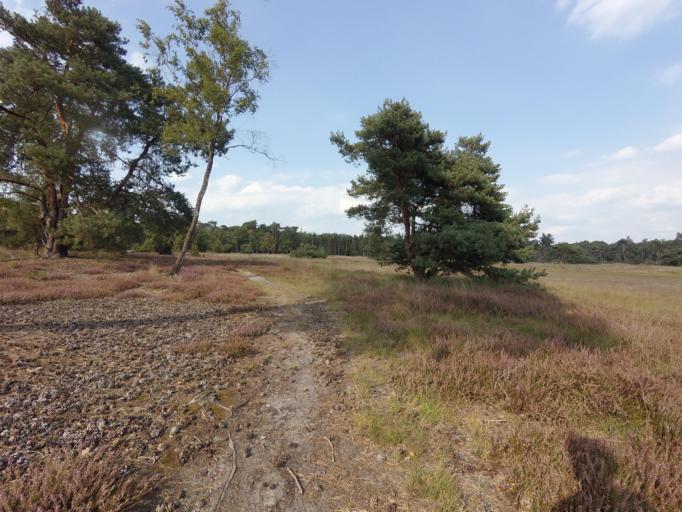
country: NL
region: North Brabant
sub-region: Gemeente Someren
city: Someren
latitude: 51.3868
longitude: 5.6539
